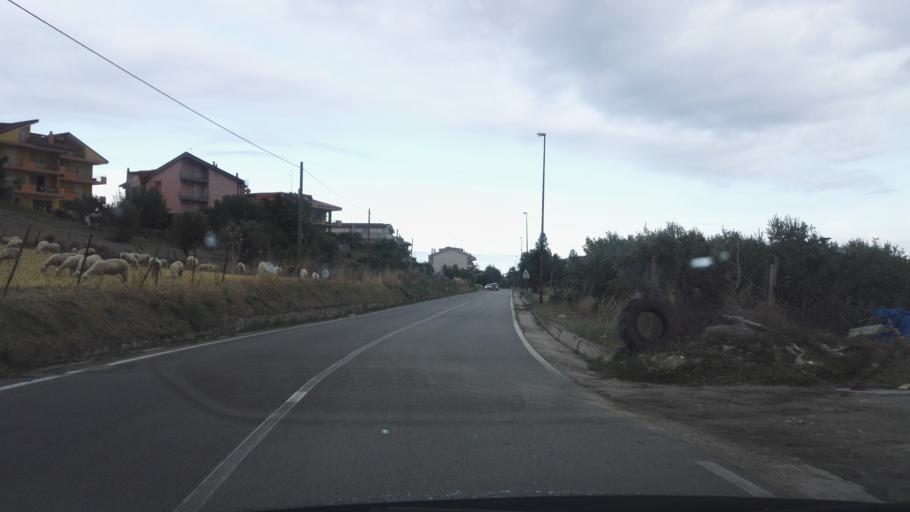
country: IT
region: Calabria
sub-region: Provincia di Catanzaro
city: Badolato Marina
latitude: 38.5734
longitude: 16.5573
